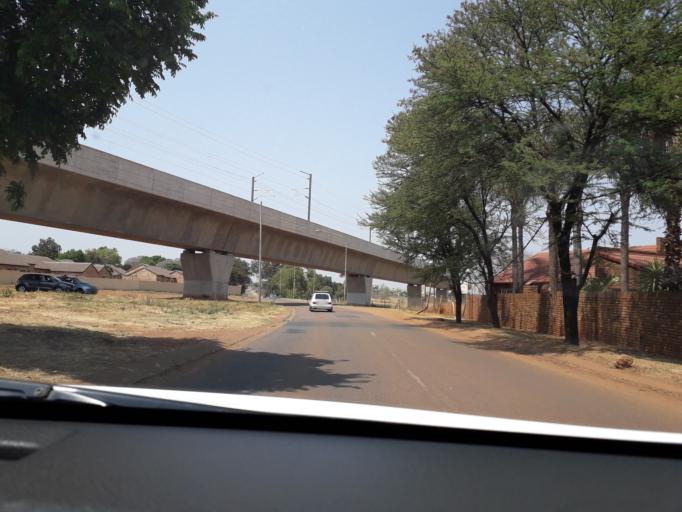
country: ZA
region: Gauteng
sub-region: City of Tshwane Metropolitan Municipality
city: Centurion
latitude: -25.8456
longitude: 28.1851
